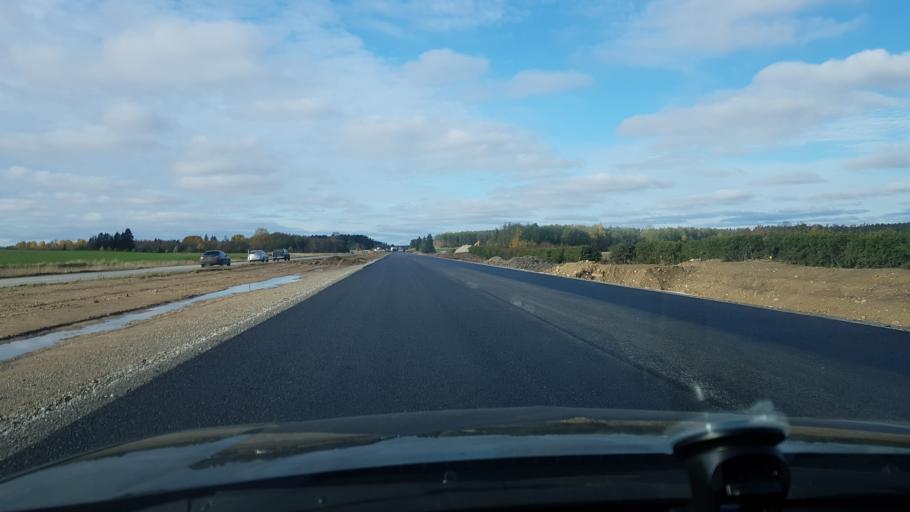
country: EE
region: Laeaene-Virumaa
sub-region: Kadrina vald
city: Kadrina
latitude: 59.4428
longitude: 26.1058
